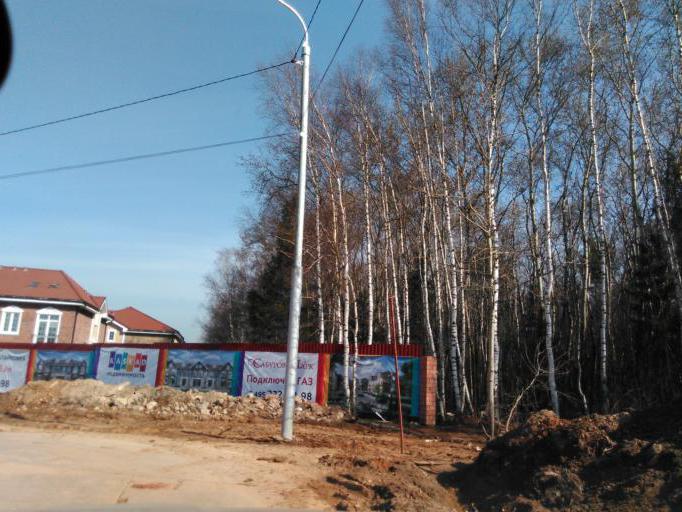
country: RU
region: Moskovskaya
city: Opalikha
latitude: 55.8749
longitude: 37.2602
